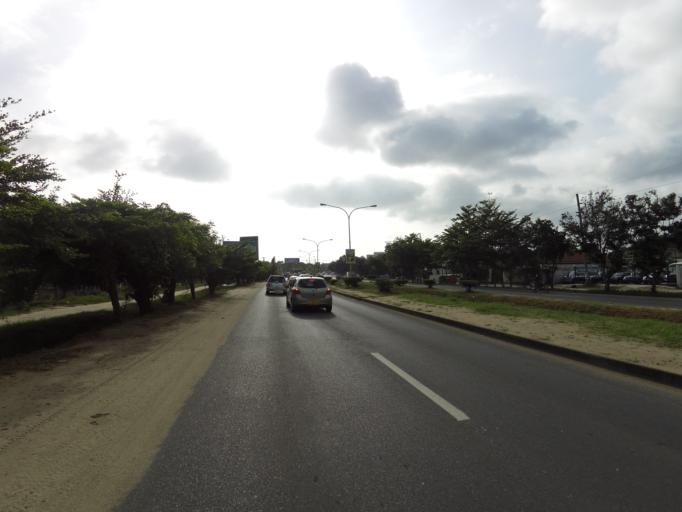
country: TZ
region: Dar es Salaam
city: Magomeni
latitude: -6.7778
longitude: 39.2690
